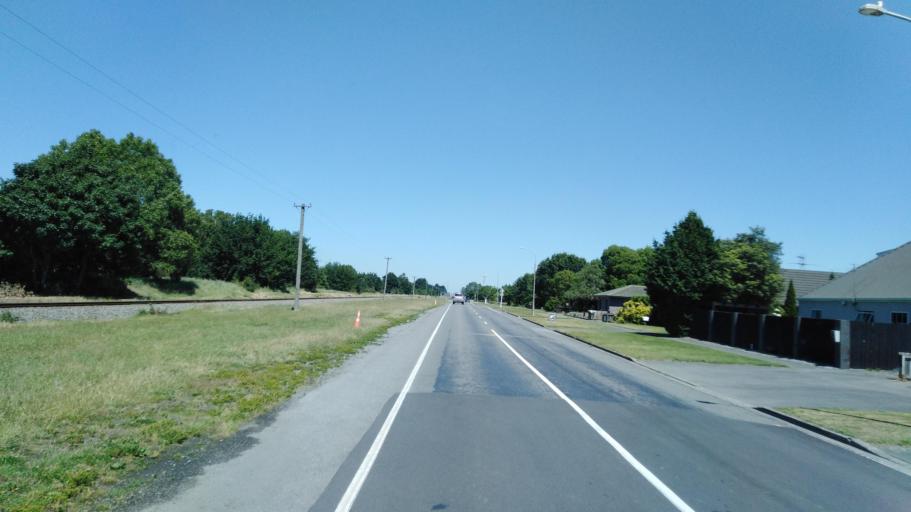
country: NZ
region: Canterbury
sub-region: Selwyn District
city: Prebbleton
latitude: -43.5554
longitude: 172.4708
